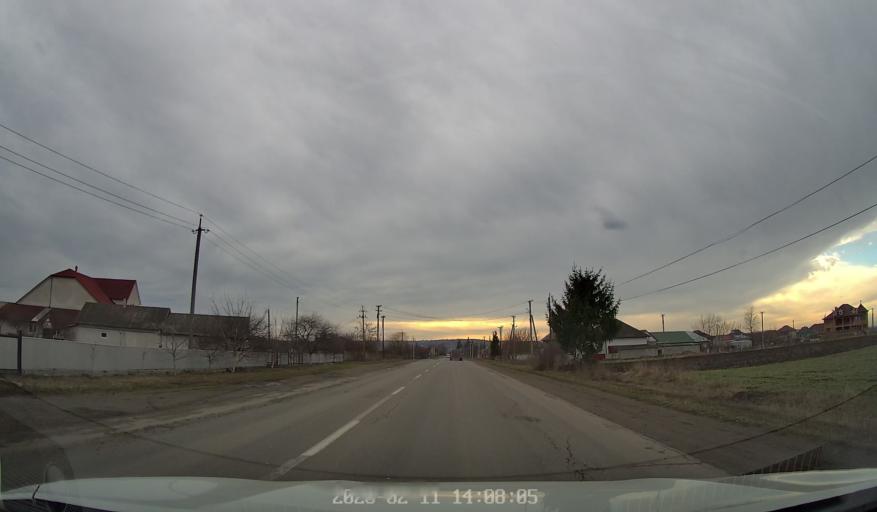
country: RO
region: Botosani
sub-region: Comuna Darabani
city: Bajura
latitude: 48.2409
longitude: 26.5480
